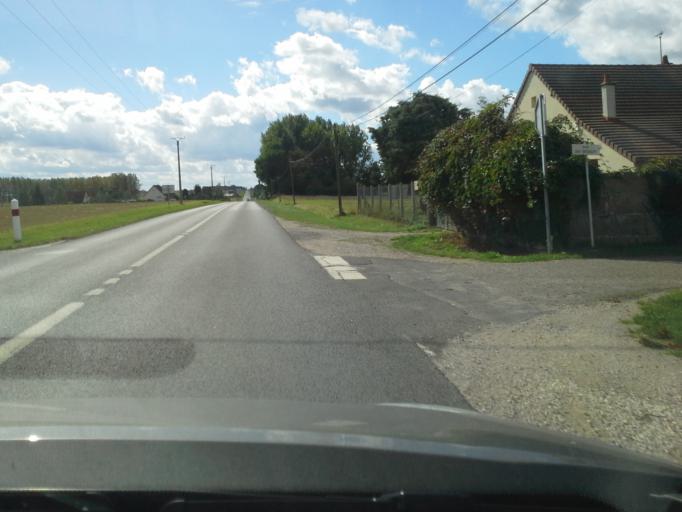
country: FR
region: Centre
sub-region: Departement du Loir-et-Cher
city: Pontlevoy
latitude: 47.4346
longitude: 1.2911
